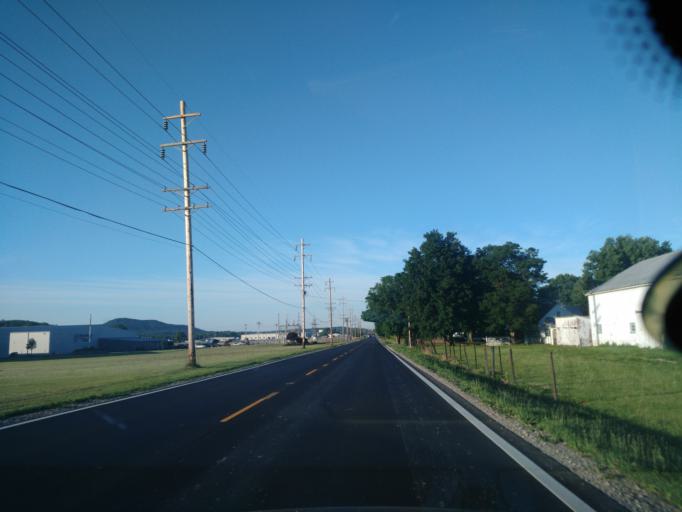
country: US
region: Ohio
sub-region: Ross County
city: Kingston
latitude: 39.4166
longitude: -82.9567
